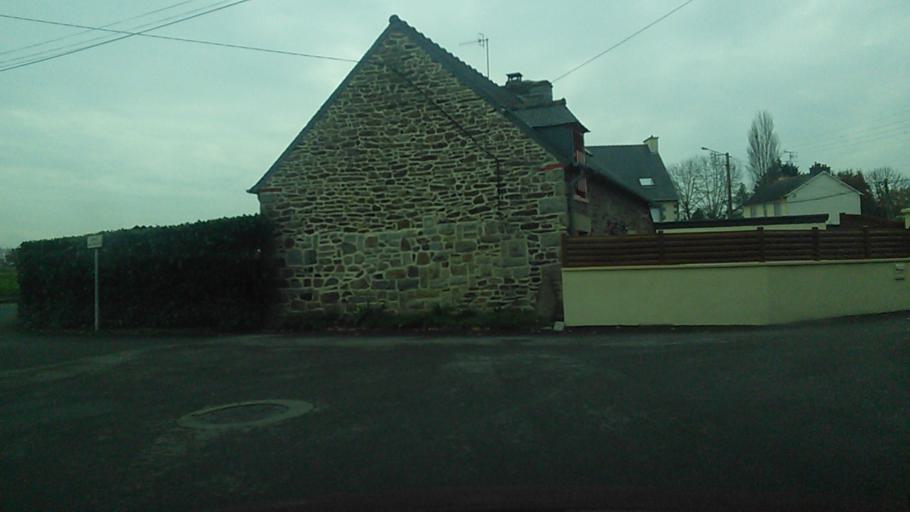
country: FR
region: Brittany
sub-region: Departement des Cotes-d'Armor
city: Yffiniac
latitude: 48.4780
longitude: -2.6546
